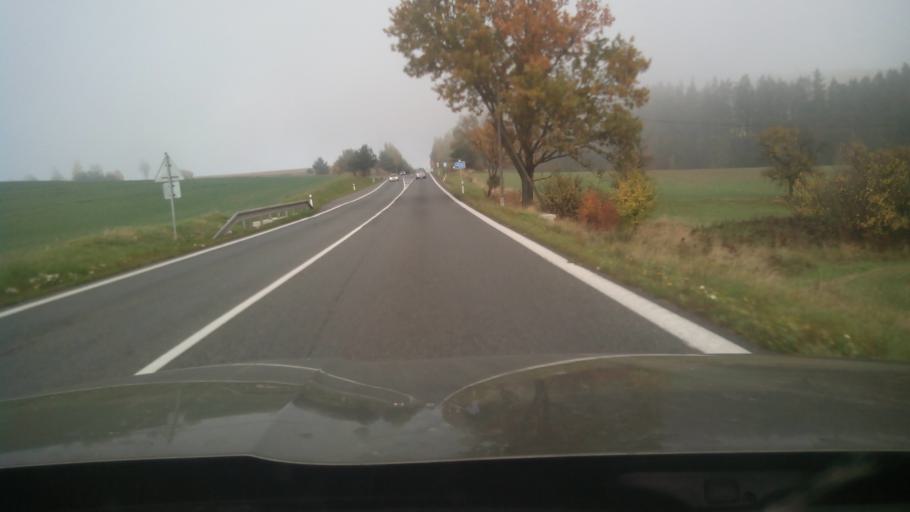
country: CZ
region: Central Bohemia
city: Milin
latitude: 49.6220
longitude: 14.0527
